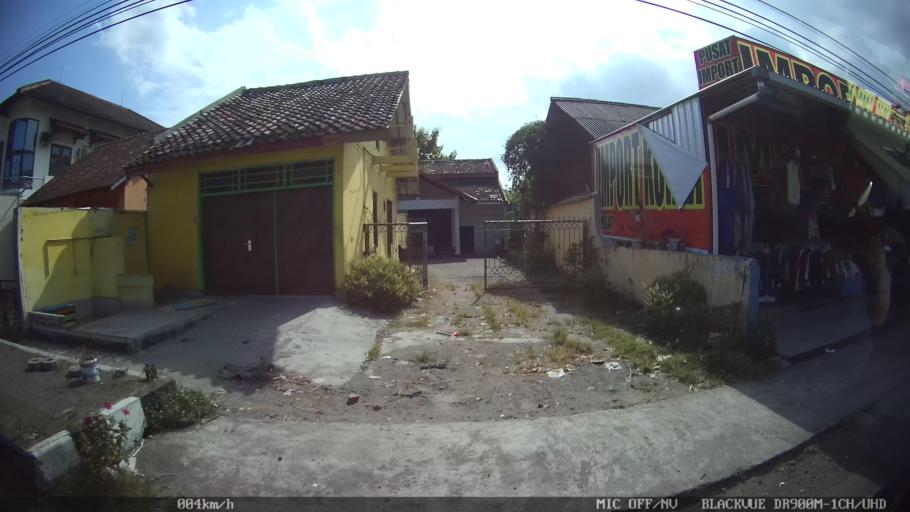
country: ID
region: Daerah Istimewa Yogyakarta
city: Sewon
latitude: -7.8381
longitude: 110.3917
